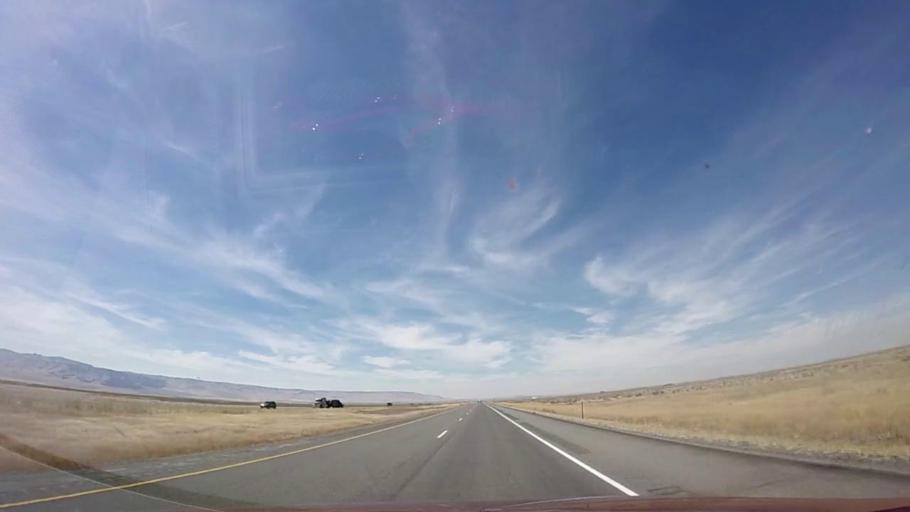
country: US
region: Idaho
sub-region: Minidoka County
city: Rupert
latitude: 42.3720
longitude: -113.2684
